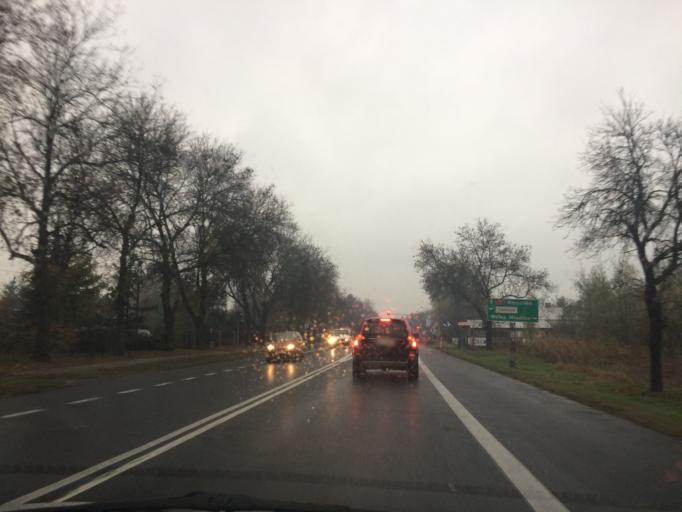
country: PL
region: Masovian Voivodeship
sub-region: Powiat otwocki
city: Otwock
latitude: 52.1361
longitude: 21.3364
